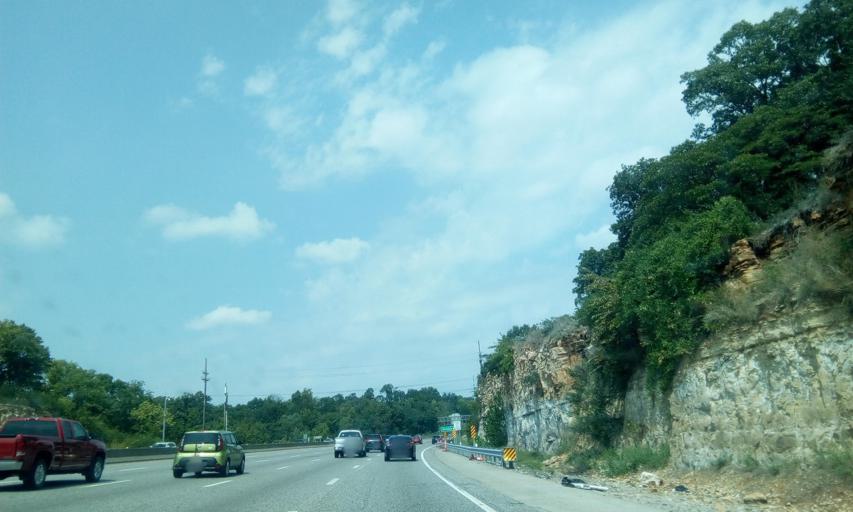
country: US
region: Missouri
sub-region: Saint Louis County
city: Sunset Hills
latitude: 38.5614
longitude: -90.4385
